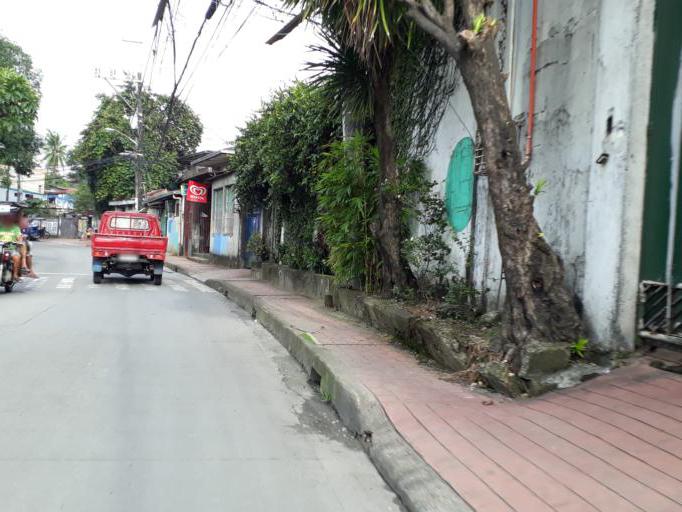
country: PH
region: Calabarzon
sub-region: Province of Rizal
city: Valenzuela
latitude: 14.6768
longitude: 120.9881
